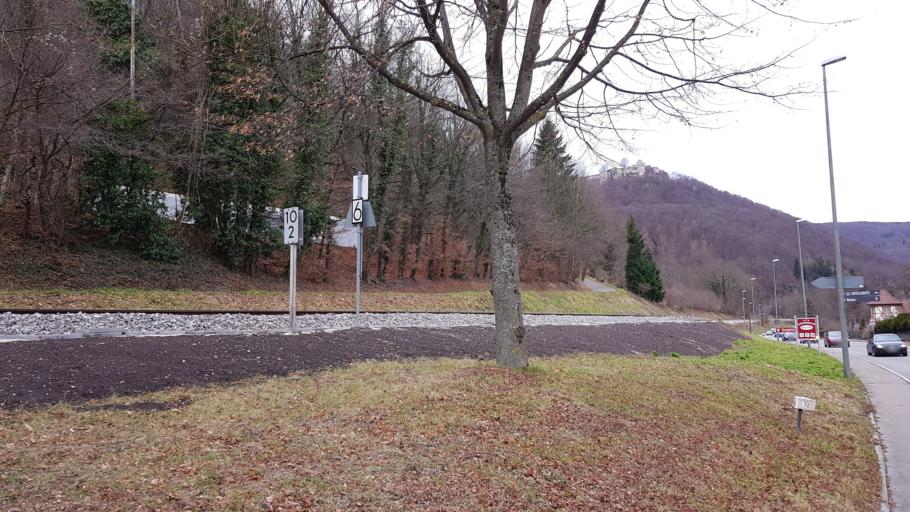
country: DE
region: Baden-Wuerttemberg
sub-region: Tuebingen Region
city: Bad Urach
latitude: 48.4926
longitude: 9.3940
